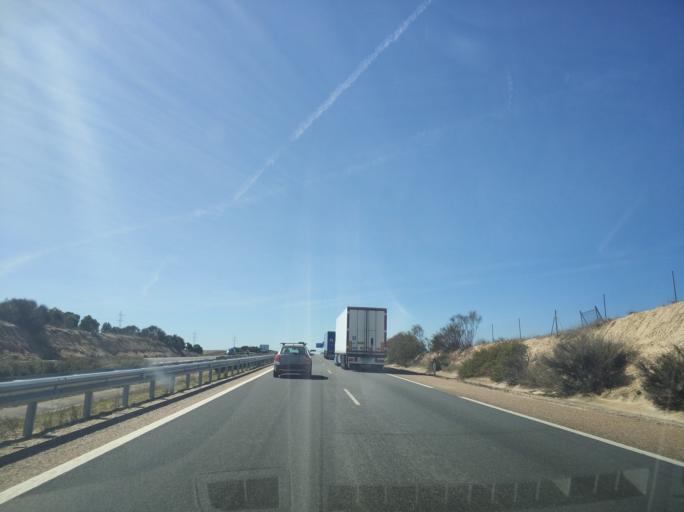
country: ES
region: Castille and Leon
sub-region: Provincia de Salamanca
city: Castellanos de Moriscos
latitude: 41.0077
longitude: -5.5988
